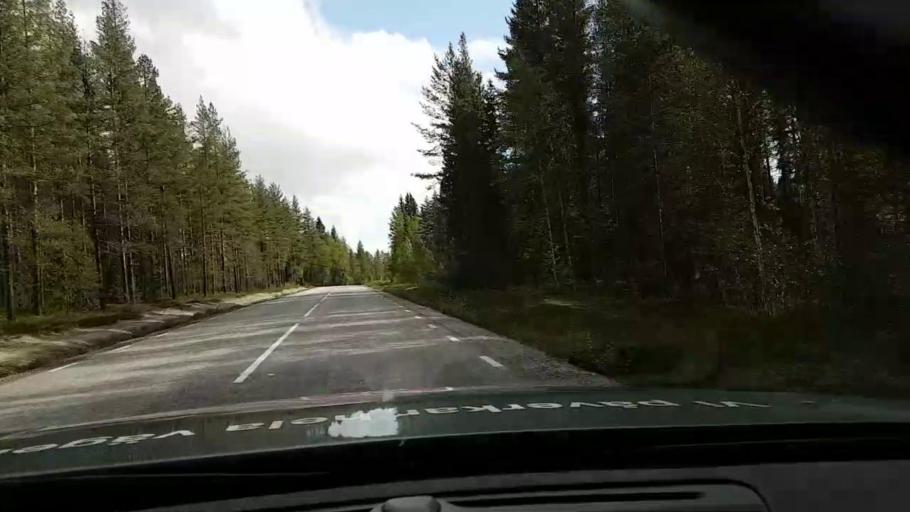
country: SE
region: Vaesternorrland
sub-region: OErnskoeldsviks Kommun
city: Bredbyn
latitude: 63.6480
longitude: 17.8936
